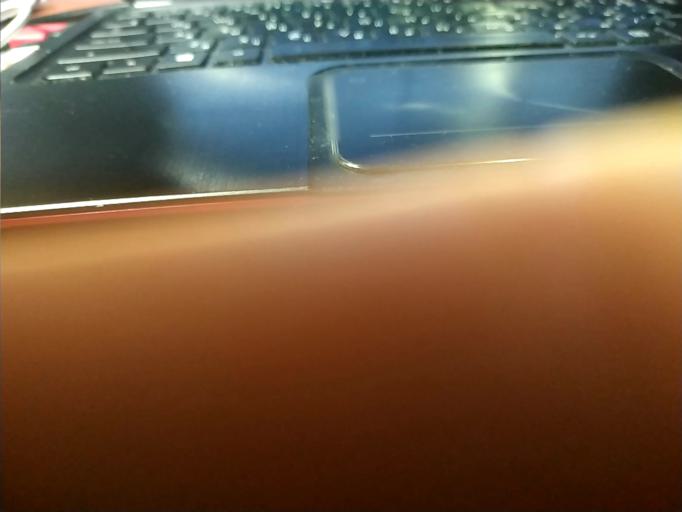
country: RU
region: Tverskaya
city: Kalashnikovo
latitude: 57.2114
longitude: 35.3224
